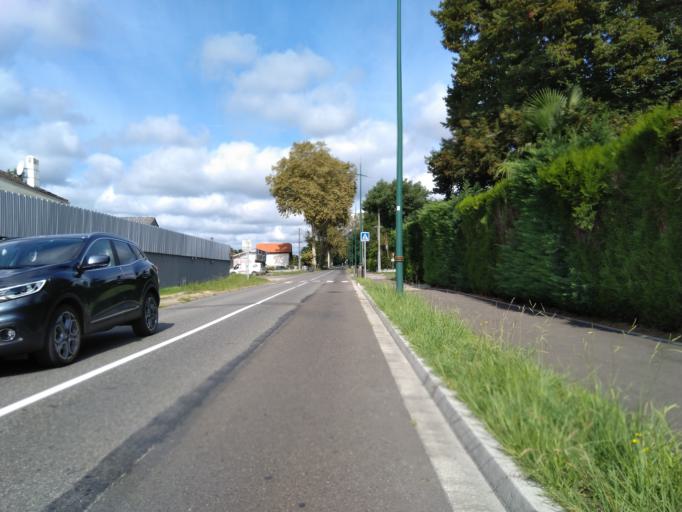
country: FR
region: Aquitaine
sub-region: Departement des Landes
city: Mees
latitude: 43.7280
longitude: -1.0864
